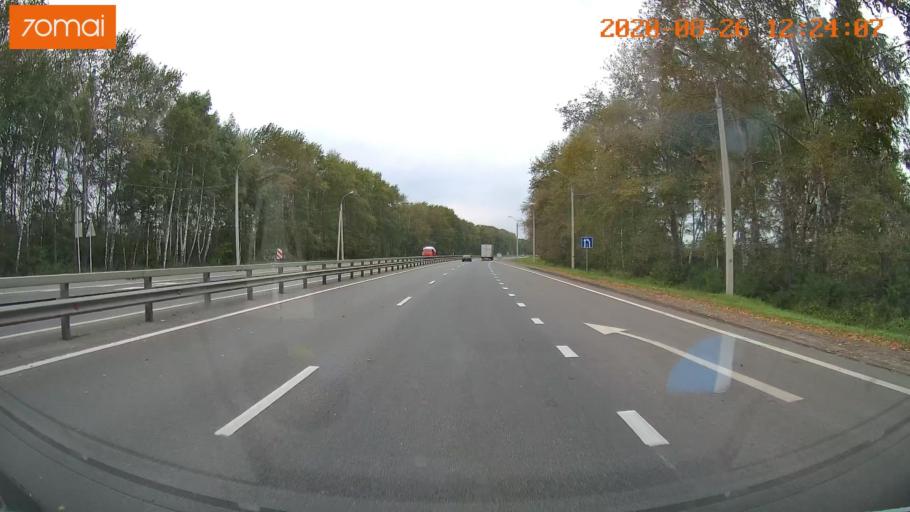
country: RU
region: Rjazan
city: Murmino
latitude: 54.5105
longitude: 39.8977
